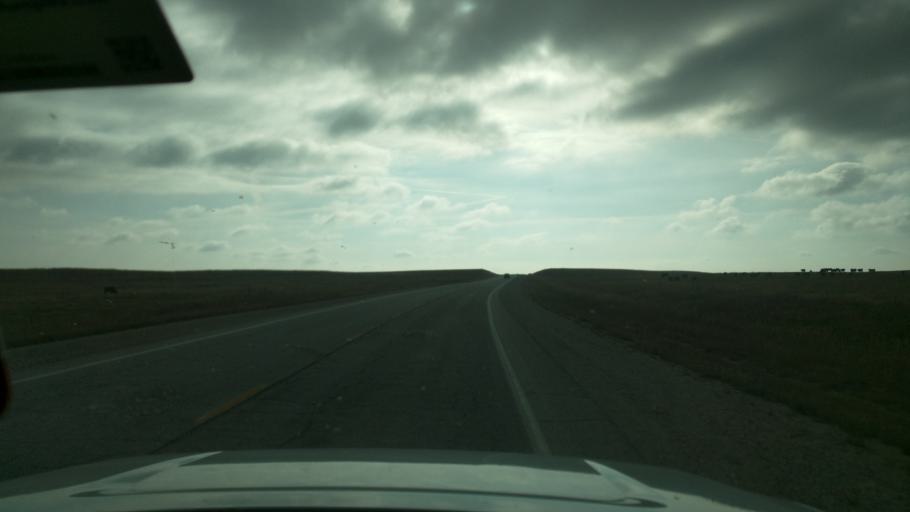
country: US
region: Kansas
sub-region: Chautauqua County
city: Sedan
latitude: 37.0993
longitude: -96.2340
